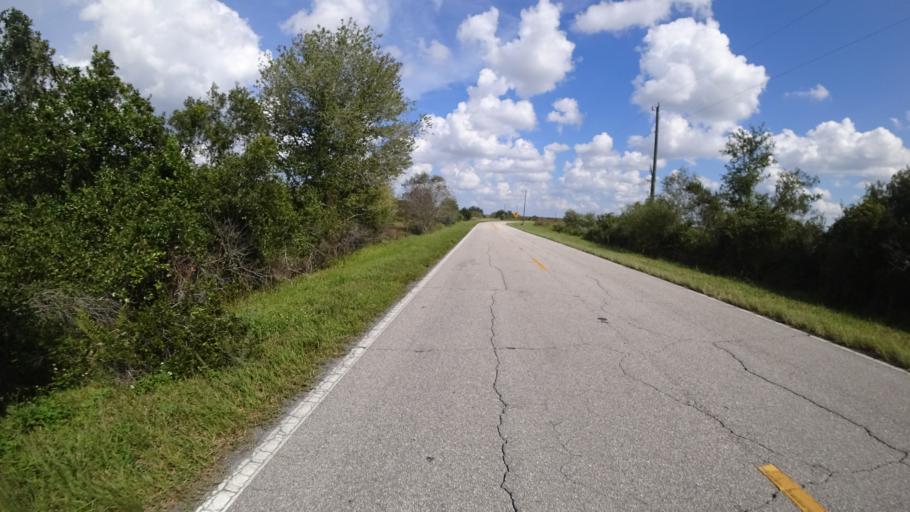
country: US
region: Florida
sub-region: Hardee County
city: Wauchula
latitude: 27.5373
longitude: -82.0829
